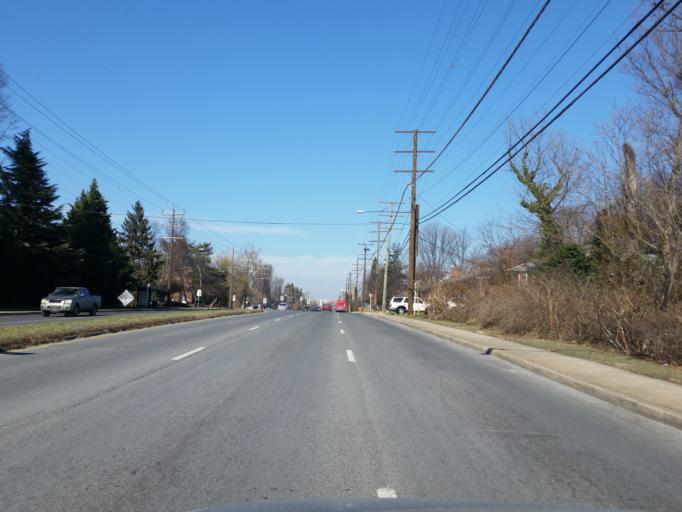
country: US
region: Maryland
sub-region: Montgomery County
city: Forest Glen
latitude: 39.0172
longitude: -77.0431
